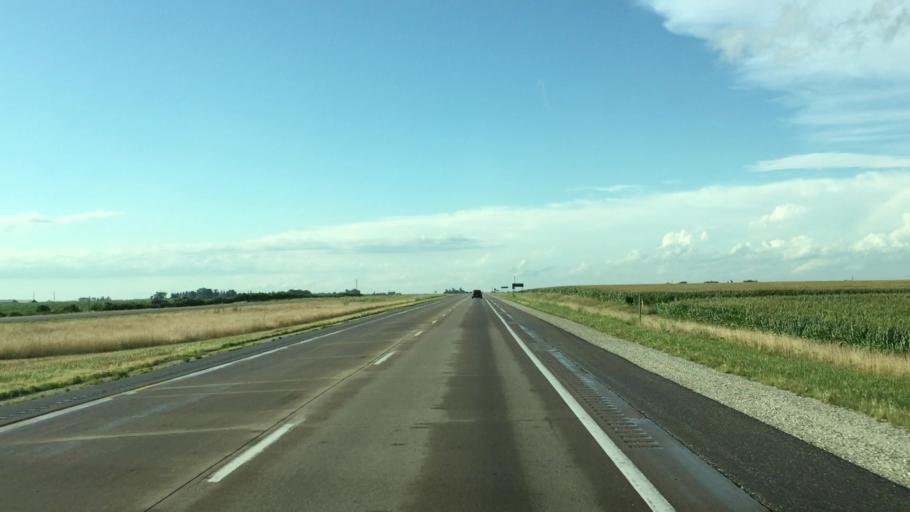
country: US
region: Iowa
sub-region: Henry County
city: Winfield
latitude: 41.1373
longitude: -91.5398
